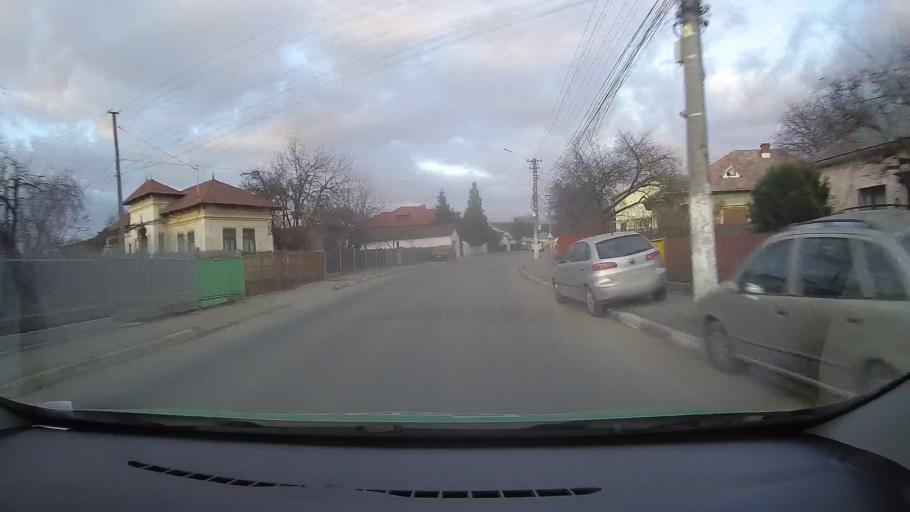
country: RO
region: Dambovita
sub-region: Municipiul Moreni
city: Moreni
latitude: 44.9945
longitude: 25.6465
